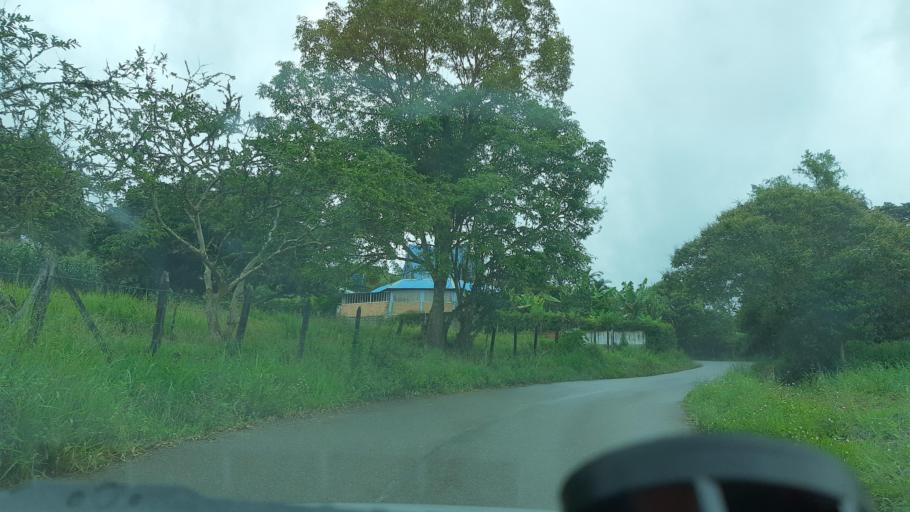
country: CO
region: Cundinamarca
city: Manta
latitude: 5.0421
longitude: -73.5134
